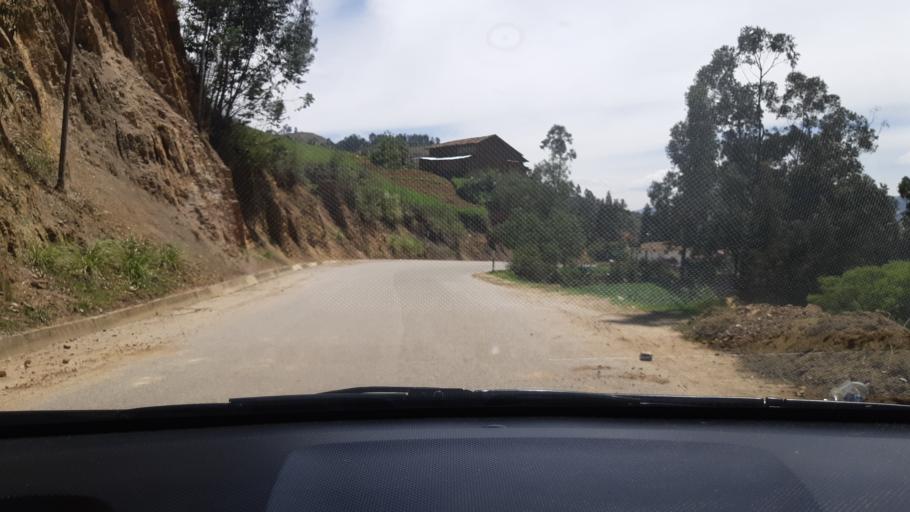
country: PE
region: Cajamarca
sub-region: Provincia de Cajamarca
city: Llacanora
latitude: -7.1923
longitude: -78.4289
